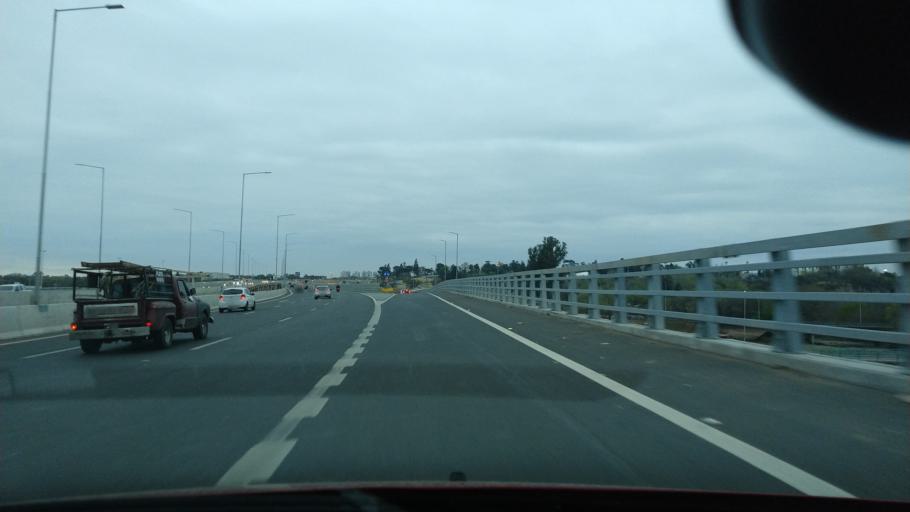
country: AR
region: Cordoba
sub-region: Departamento de Capital
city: Cordoba
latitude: -31.3668
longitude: -64.2499
